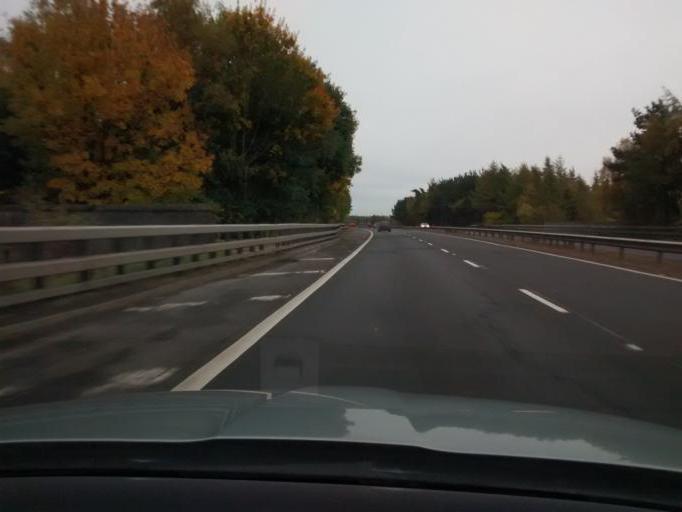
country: GB
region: Scotland
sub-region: Stirling
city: Cowie
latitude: 56.0557
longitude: -3.8479
